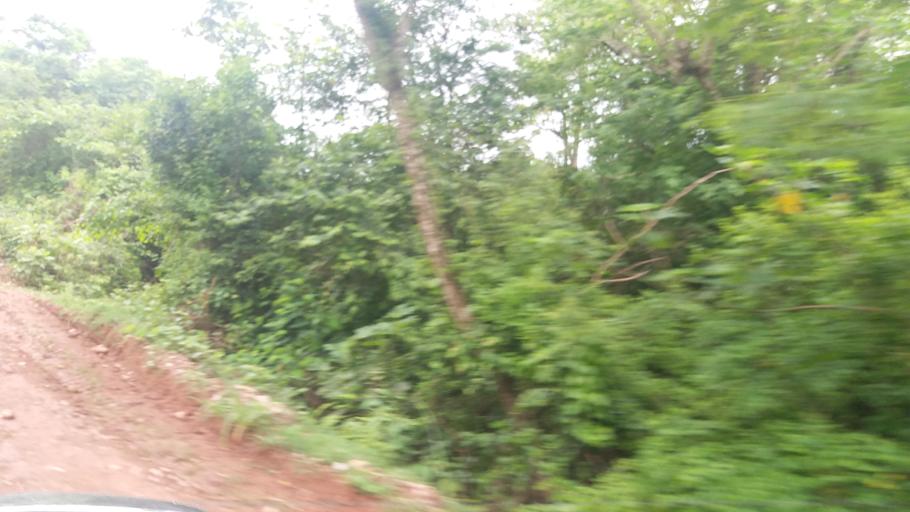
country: BO
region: Tarija
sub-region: Provincia Gran Chaco
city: Yacuiba
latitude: -21.8310
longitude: -63.7193
